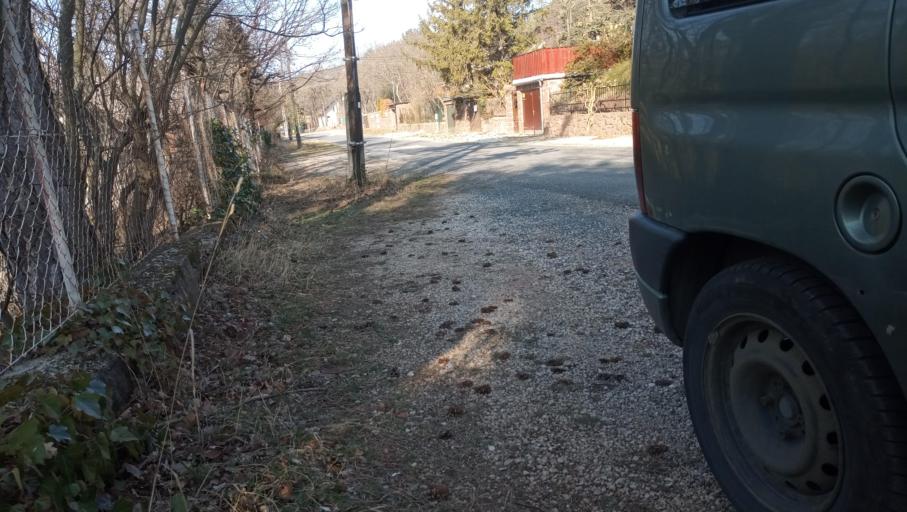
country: HU
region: Veszprem
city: Balatonalmadi
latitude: 47.0126
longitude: 18.0012
